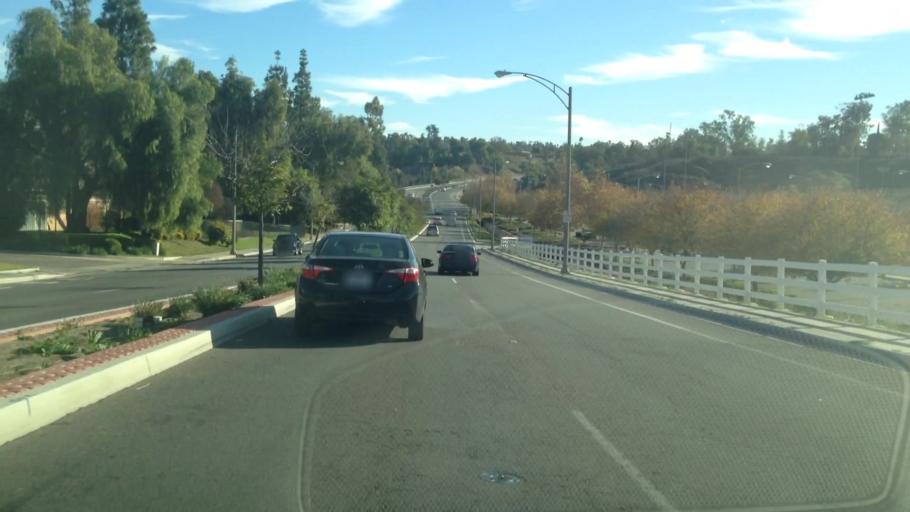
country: US
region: California
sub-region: Riverside County
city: Riverside
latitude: 33.9591
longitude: -117.3476
